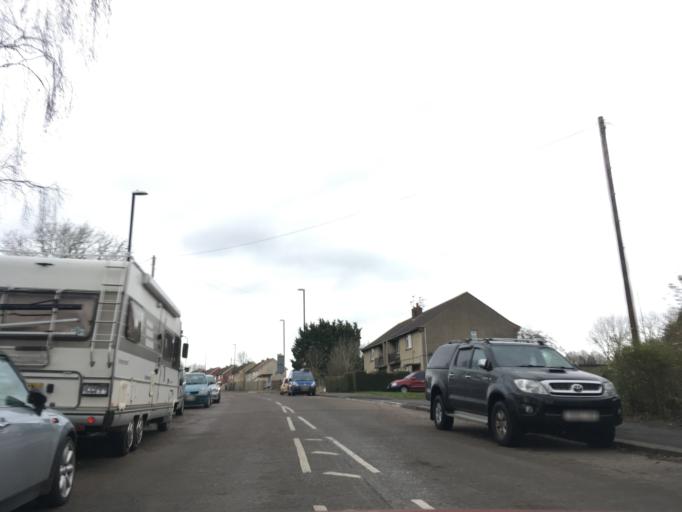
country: GB
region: England
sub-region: South Gloucestershire
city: Stoke Gifford
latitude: 51.4875
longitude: -2.5635
